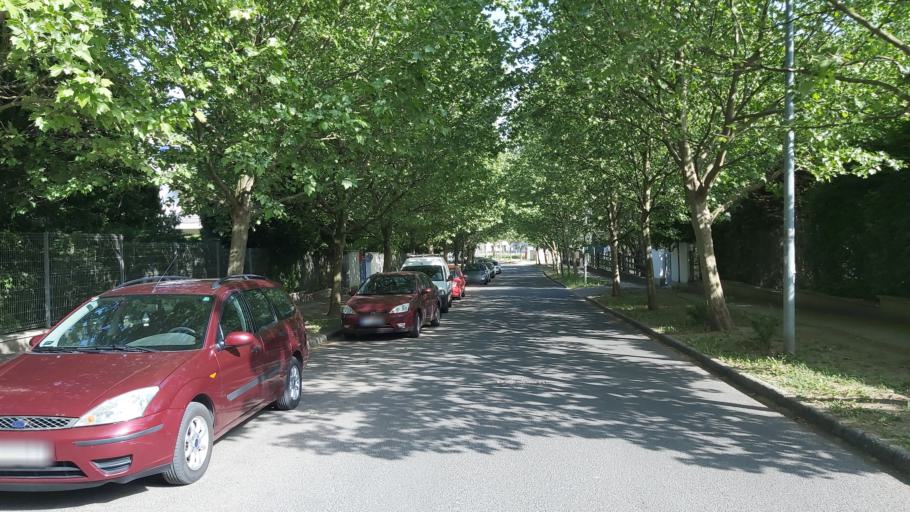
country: HU
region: Budapest
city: Budapest XXII. keruelet
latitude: 47.4455
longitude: 19.0087
